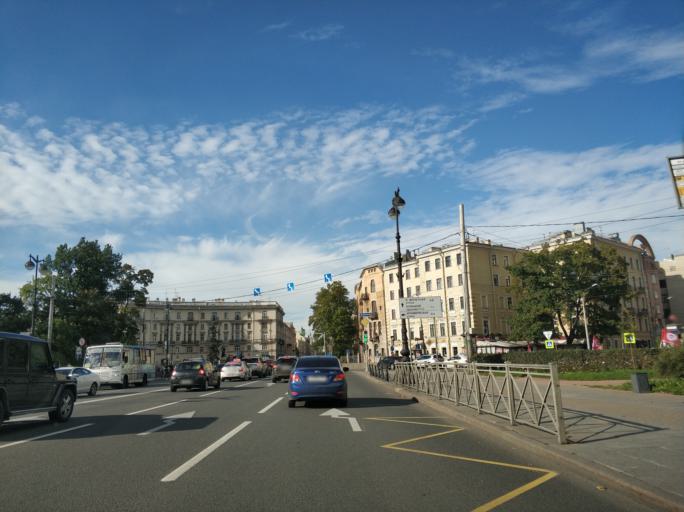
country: RU
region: St.-Petersburg
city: Petrogradka
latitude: 59.9556
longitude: 30.3216
